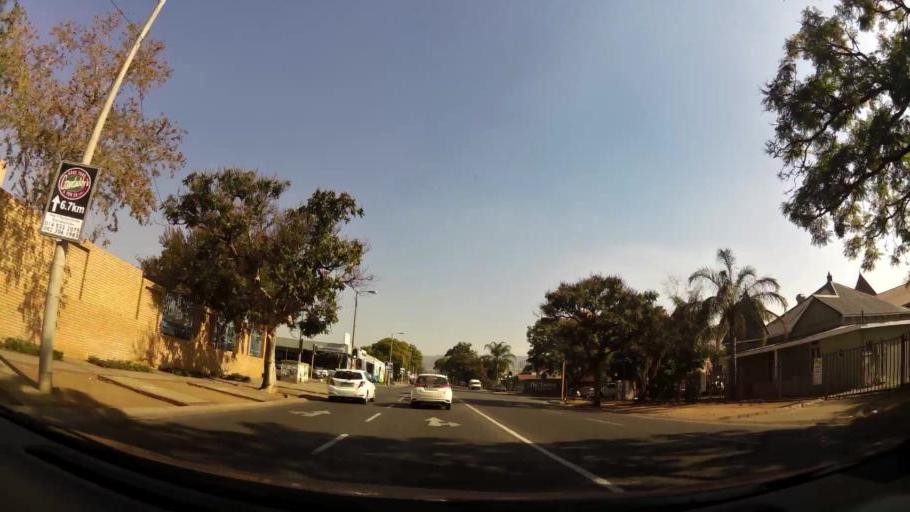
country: ZA
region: North-West
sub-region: Bojanala Platinum District Municipality
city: Rustenburg
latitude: -25.6743
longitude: 27.2414
